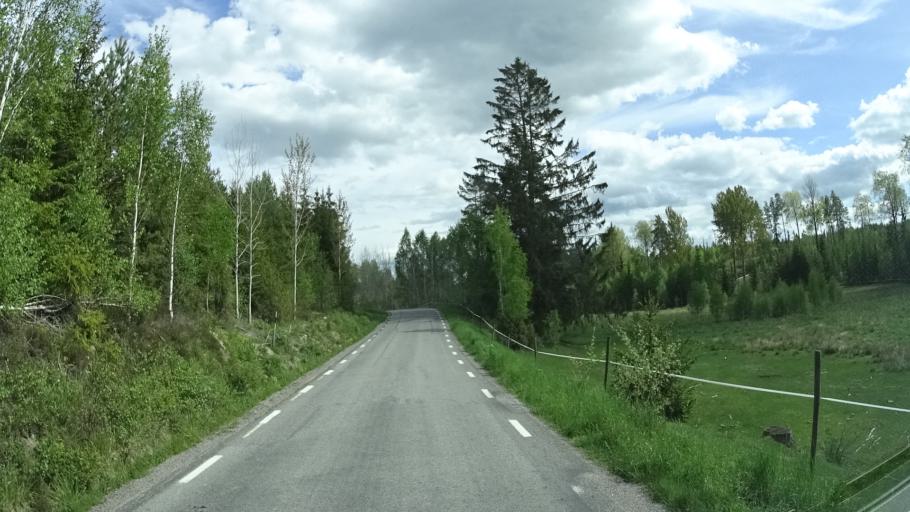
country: SE
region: OEstergoetland
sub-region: Finspangs Kommun
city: Finspang
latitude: 58.6099
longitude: 15.7351
